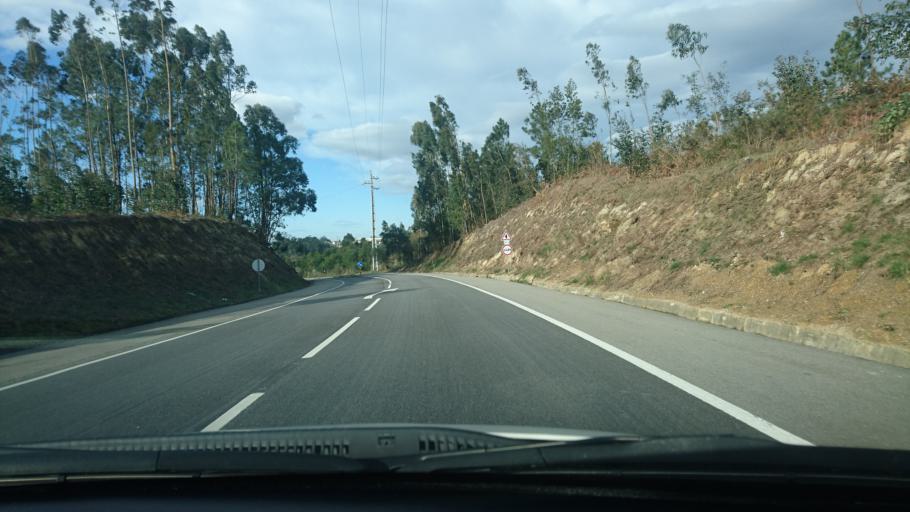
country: PT
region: Aveiro
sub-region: Santa Maria da Feira
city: Rio Meao
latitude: 40.9612
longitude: -8.5898
